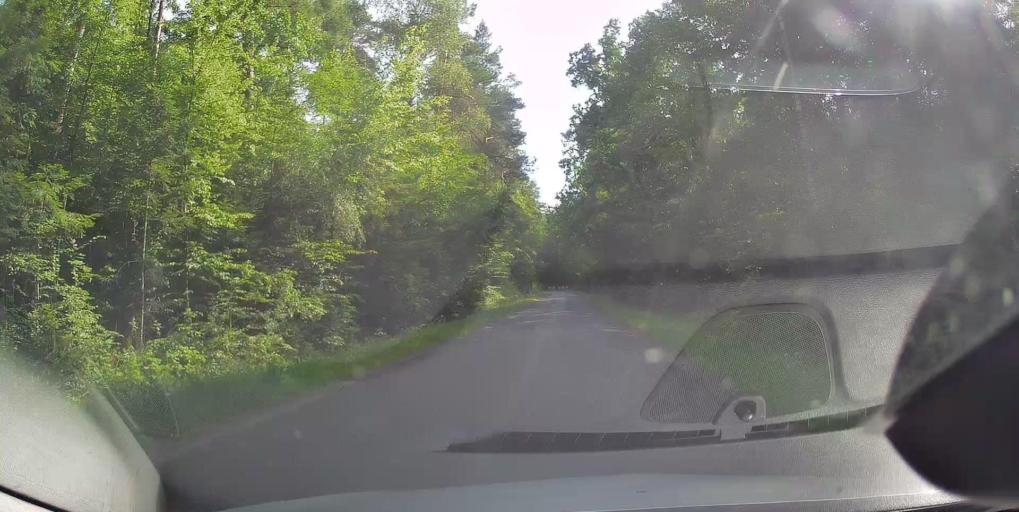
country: PL
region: Lodz Voivodeship
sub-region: Powiat opoczynski
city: Mniszkow
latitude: 51.4395
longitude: 20.0243
